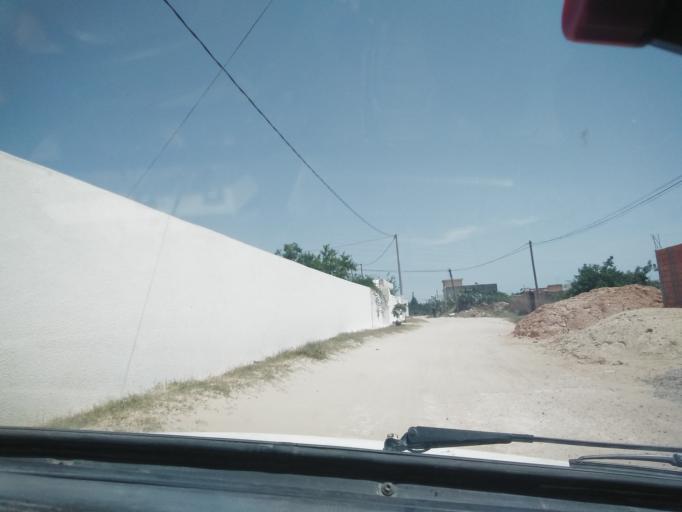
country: TN
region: Safaqis
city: Al Qarmadah
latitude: 34.8034
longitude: 10.7749
